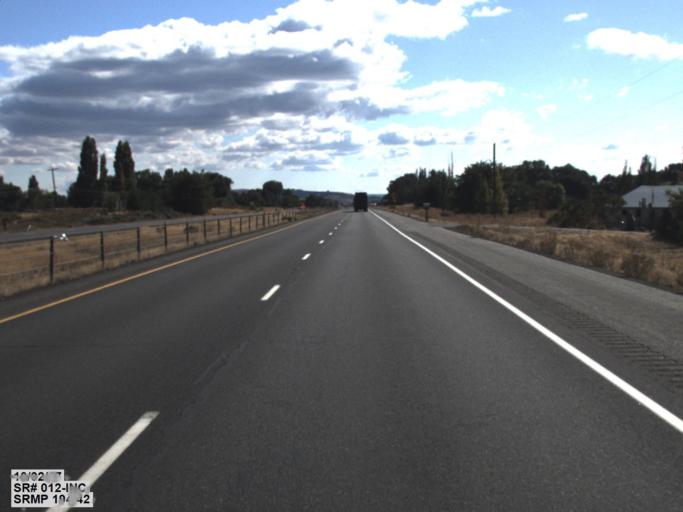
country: US
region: Washington
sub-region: Yakima County
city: Gleed
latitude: 46.6785
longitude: -120.6452
